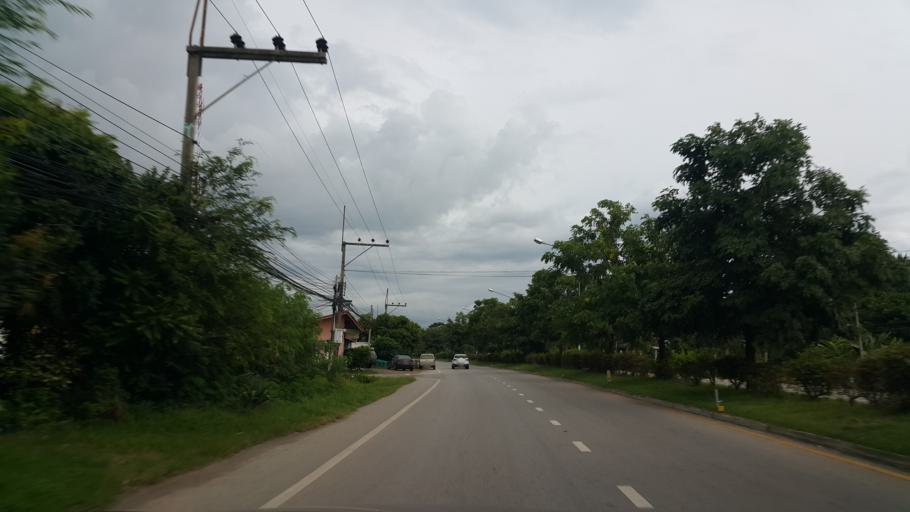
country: TH
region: Phayao
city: Dok Kham Tai
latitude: 19.1660
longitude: 100.0010
